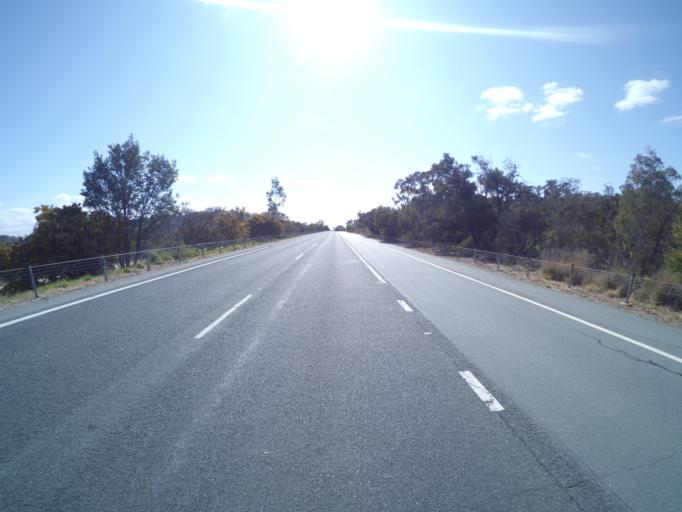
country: AU
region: Australian Capital Territory
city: Kaleen
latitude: -35.2175
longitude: 149.1825
